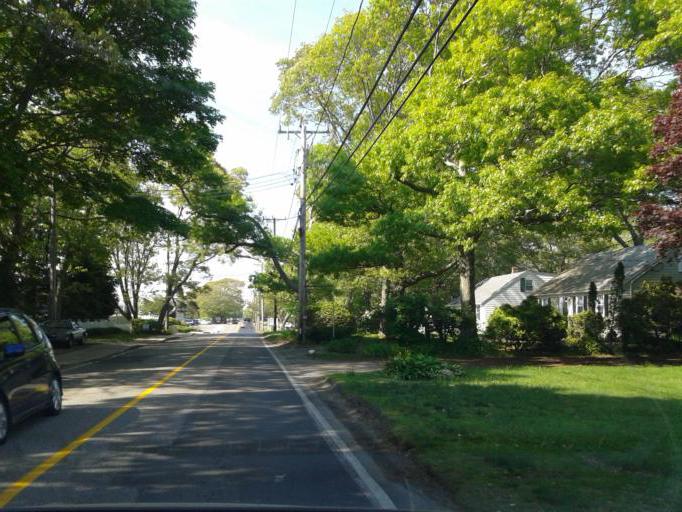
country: US
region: Massachusetts
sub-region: Barnstable County
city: Falmouth
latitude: 41.5486
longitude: -70.6000
